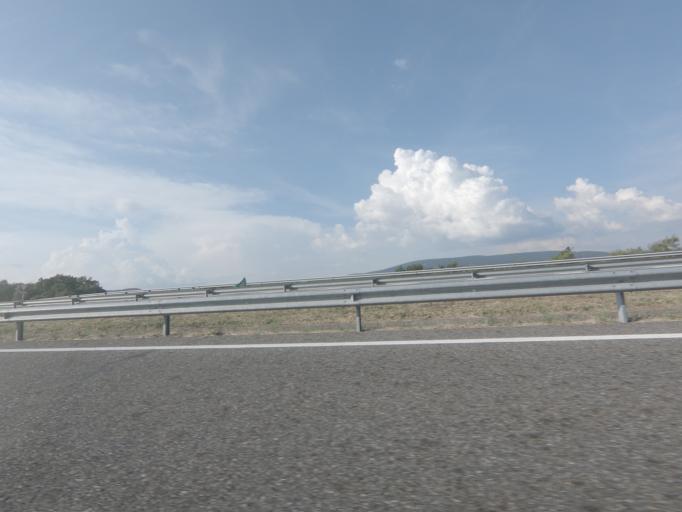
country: ES
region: Galicia
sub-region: Provincia de Ourense
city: Cualedro
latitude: 41.9805
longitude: -7.5400
